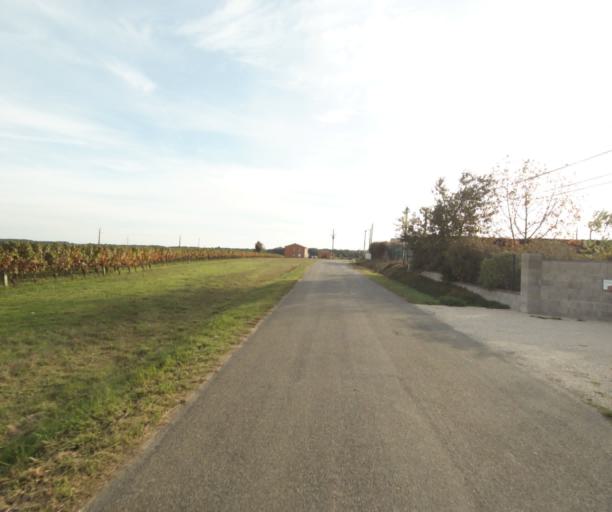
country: FR
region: Midi-Pyrenees
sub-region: Departement du Tarn-et-Garonne
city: Campsas
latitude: 43.8871
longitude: 1.3254
